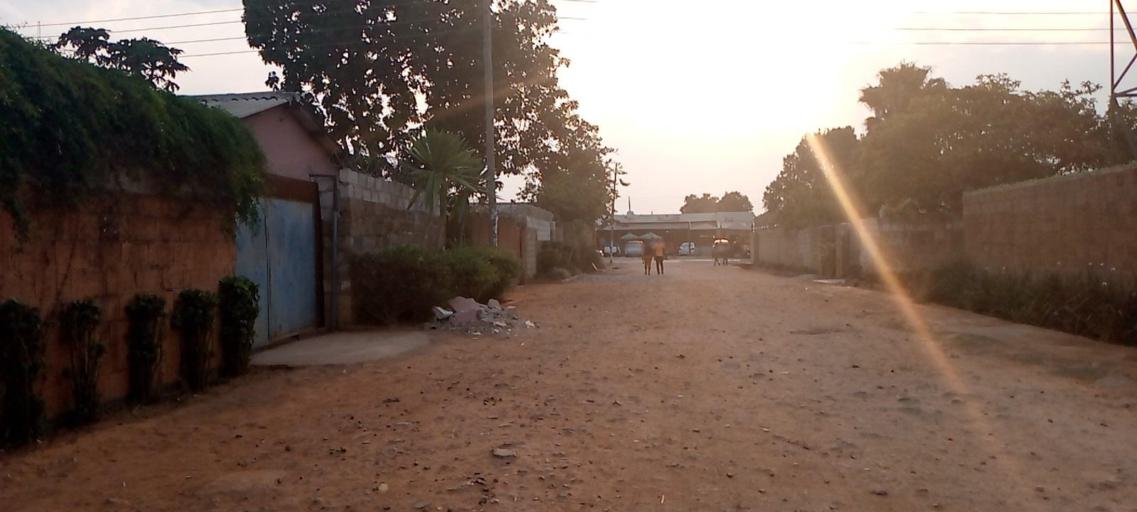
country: ZM
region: Lusaka
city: Lusaka
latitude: -15.4071
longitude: 28.3464
